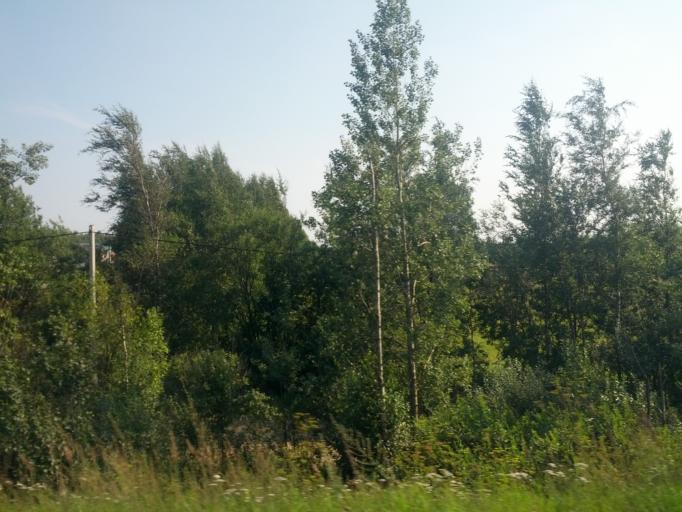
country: RU
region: Leningrad
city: Staraya
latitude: 59.8902
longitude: 30.6357
